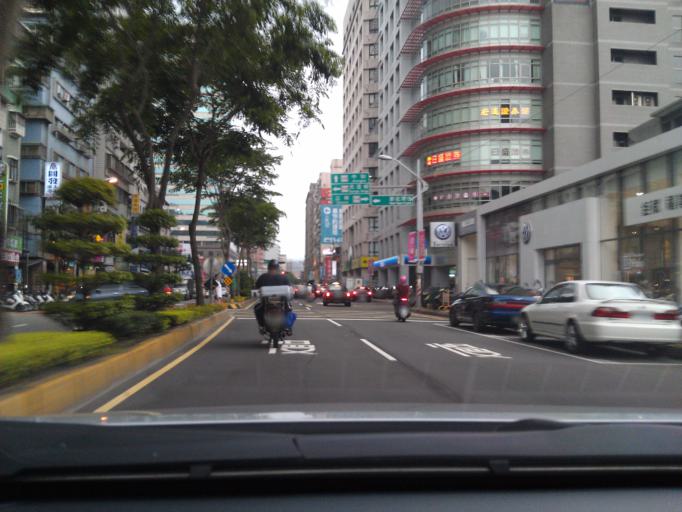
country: TW
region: Taipei
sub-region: Taipei
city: Banqiao
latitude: 25.0201
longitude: 121.4792
